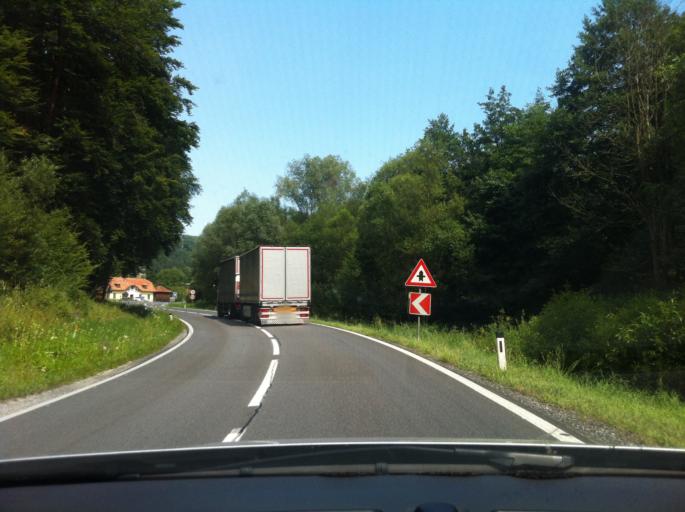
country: AT
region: Styria
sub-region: Politischer Bezirk Hartberg-Fuerstenfeld
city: Stubenberg
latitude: 47.2392
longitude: 15.7917
